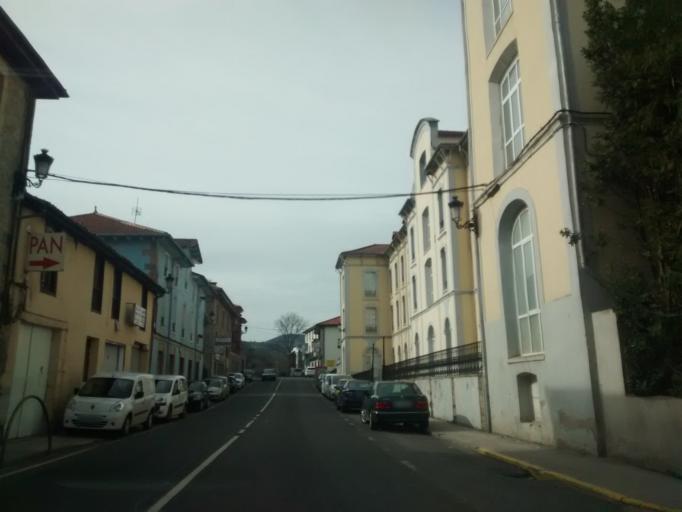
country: ES
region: Cantabria
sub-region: Provincia de Cantabria
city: Santiurde de Toranzo
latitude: 43.1974
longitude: -3.9232
